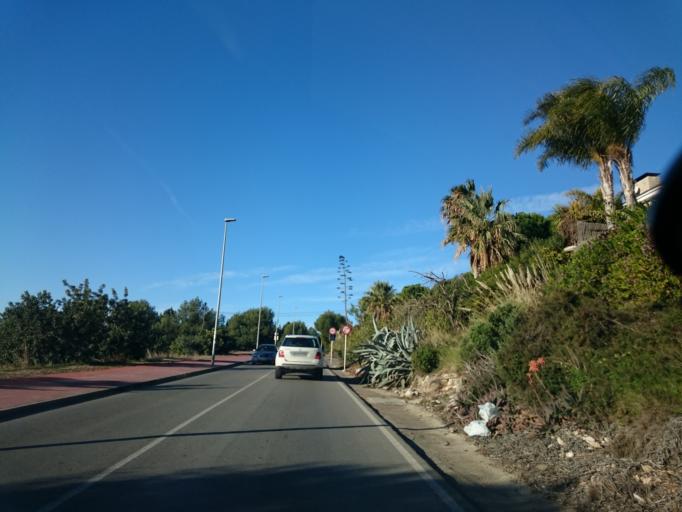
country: ES
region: Catalonia
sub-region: Provincia de Barcelona
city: Sitges
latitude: 41.2442
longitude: 1.7975
